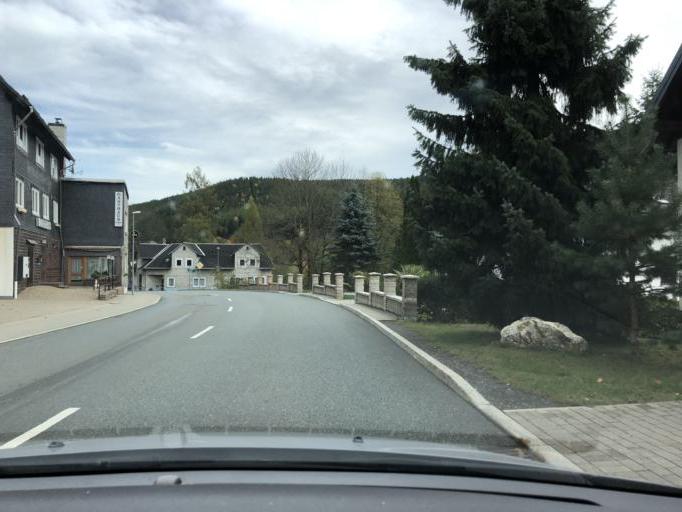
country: DE
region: Thuringia
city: Lichte
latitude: 50.5183
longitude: 11.1764
